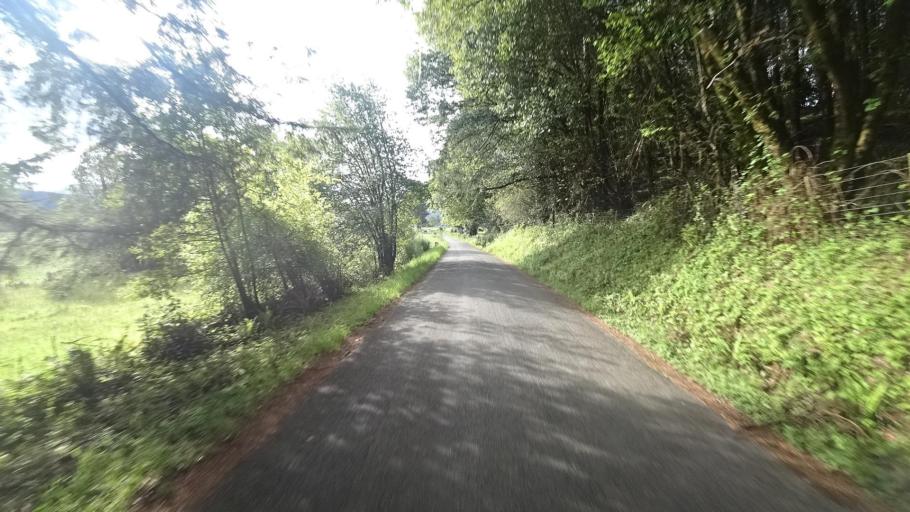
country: US
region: California
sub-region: Humboldt County
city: Blue Lake
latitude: 40.8758
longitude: -124.0108
